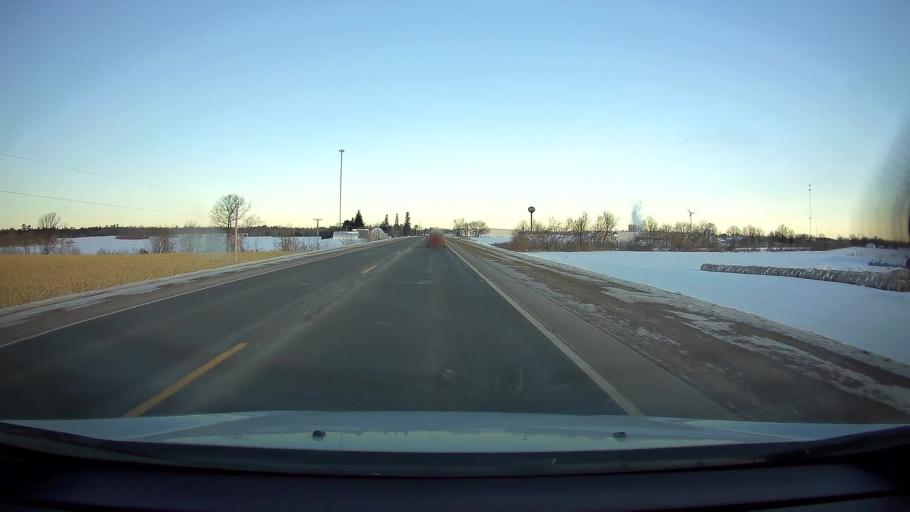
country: US
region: Wisconsin
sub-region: Barron County
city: Turtle Lake
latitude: 45.3837
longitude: -92.1667
